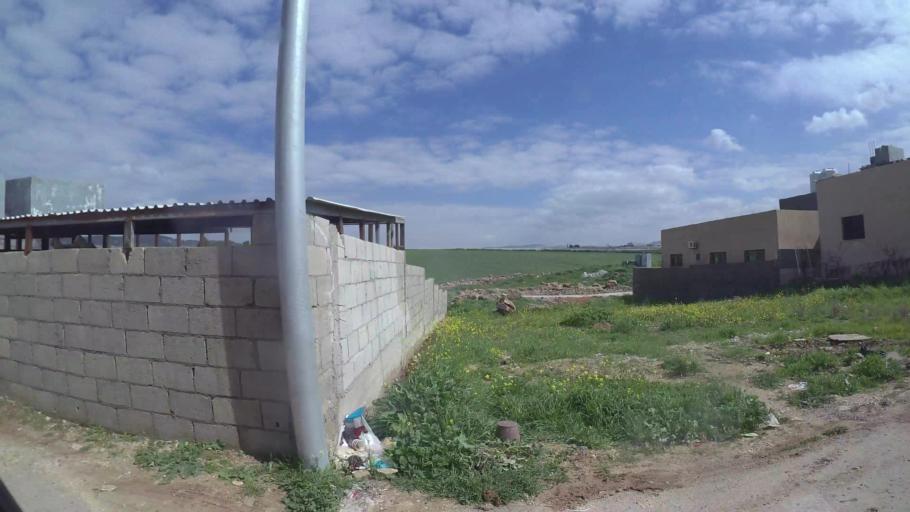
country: JO
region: Amman
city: Al Jubayhah
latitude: 32.0670
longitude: 35.8231
